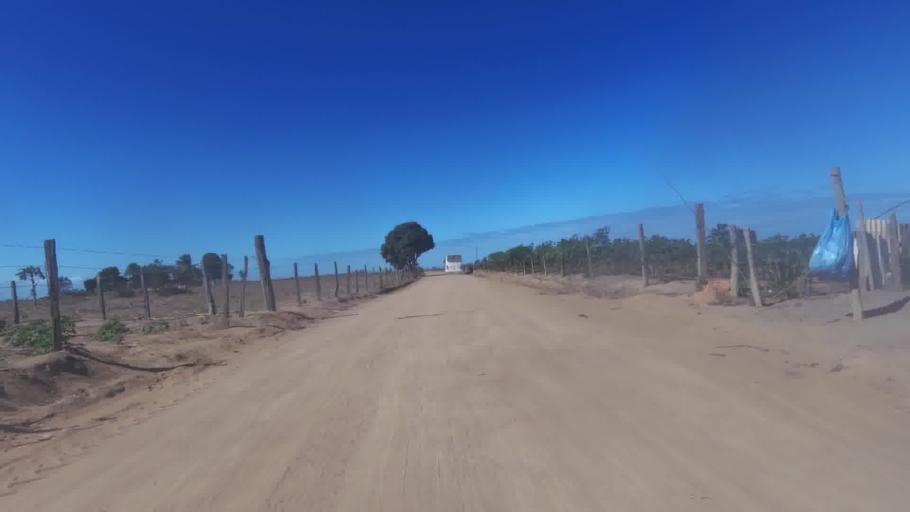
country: BR
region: Espirito Santo
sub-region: Marataizes
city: Marataizes
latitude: -21.1313
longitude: -40.9858
